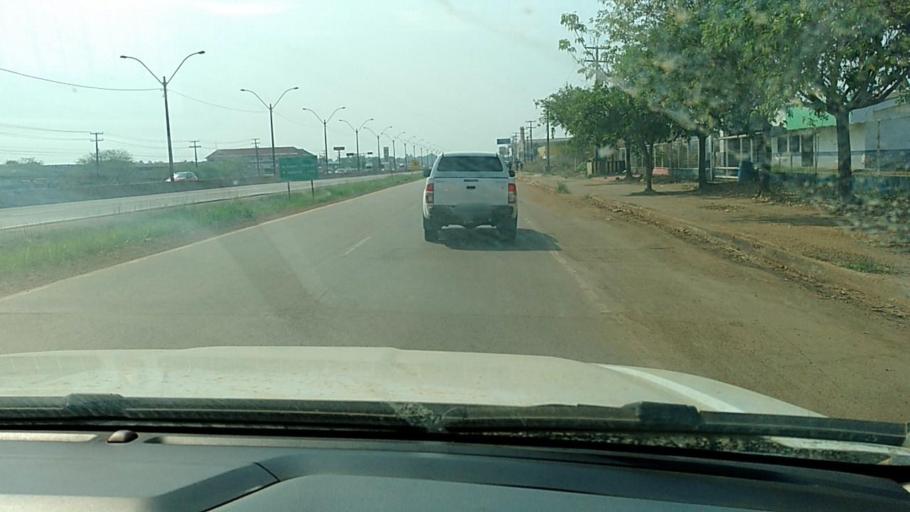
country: BR
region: Rondonia
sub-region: Porto Velho
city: Porto Velho
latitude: -8.7877
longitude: -63.8557
